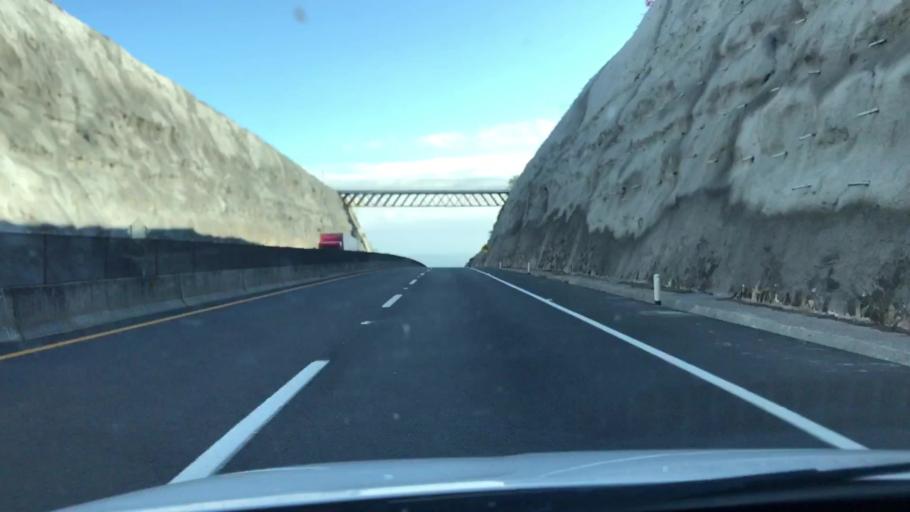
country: MX
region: Jalisco
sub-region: San Juan de los Lagos
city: Mezquitic de la Magdalena
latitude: 21.1967
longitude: -102.3418
